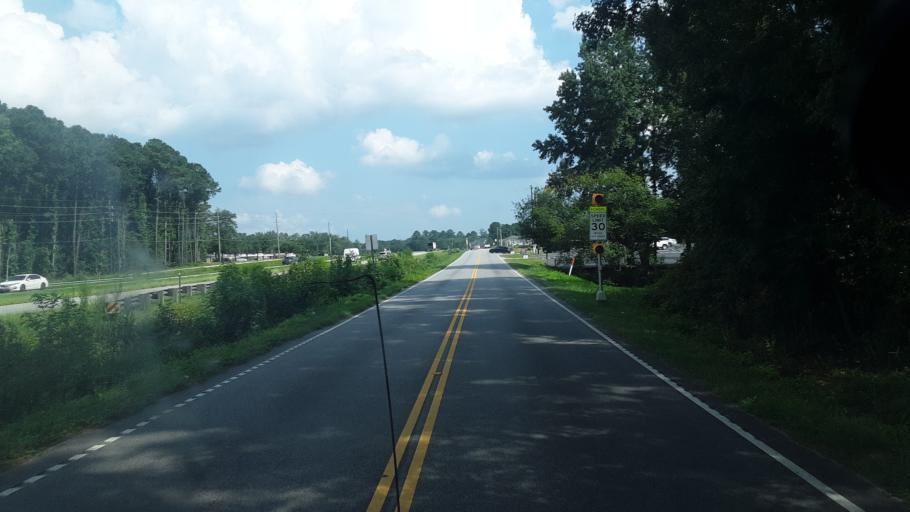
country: US
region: South Carolina
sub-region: Sumter County
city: Sumter
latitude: 33.9498
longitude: -80.3616
